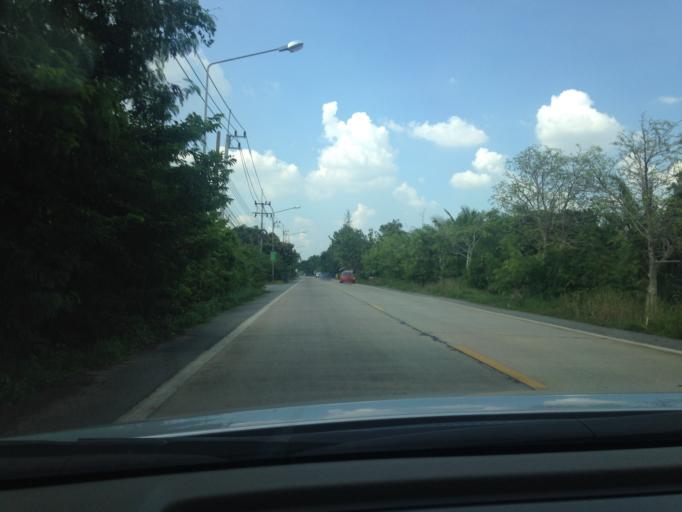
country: TH
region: Phra Nakhon Si Ayutthaya
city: Ban Bang Kadi Pathum Thani
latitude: 14.0319
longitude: 100.5932
